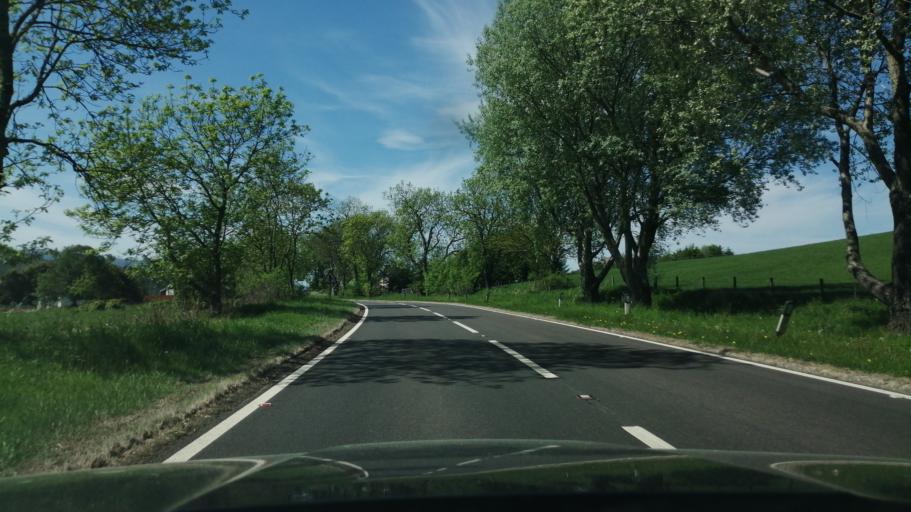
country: GB
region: Scotland
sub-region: Moray
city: Rothes
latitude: 57.4919
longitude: -3.1576
